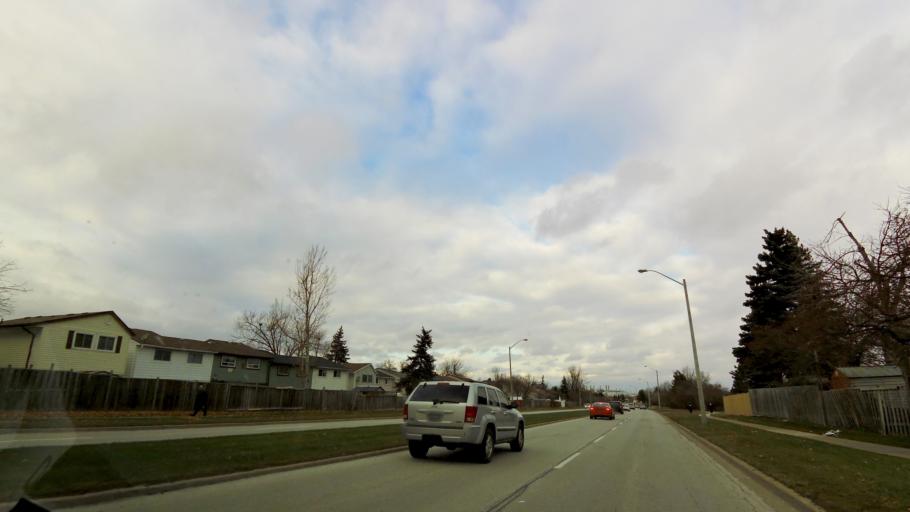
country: CA
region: Ontario
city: Brampton
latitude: 43.7393
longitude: -79.7246
